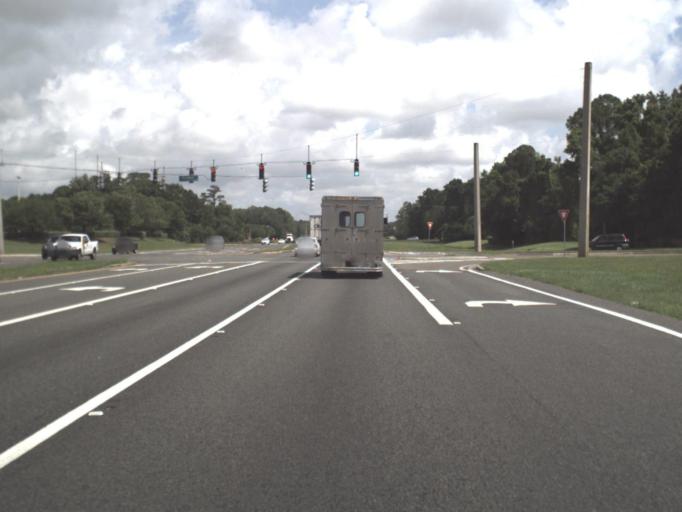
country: US
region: Florida
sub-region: Saint Johns County
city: Fruit Cove
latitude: 30.1845
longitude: -81.5516
